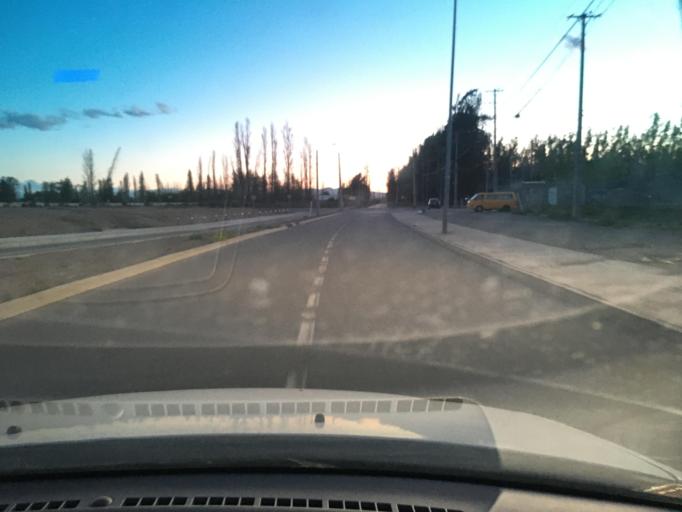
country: CL
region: Santiago Metropolitan
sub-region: Provincia de Chacabuco
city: Chicureo Abajo
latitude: -33.2904
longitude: -70.7364
